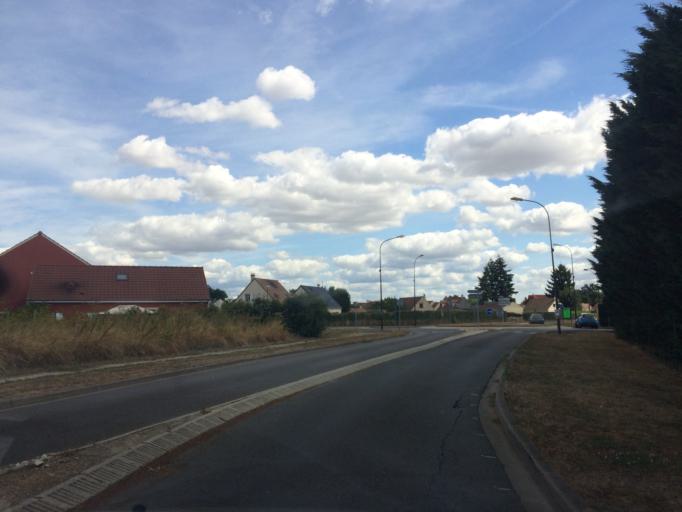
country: FR
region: Ile-de-France
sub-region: Departement de l'Essonne
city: Saint-Vrain
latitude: 48.5453
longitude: 2.3217
